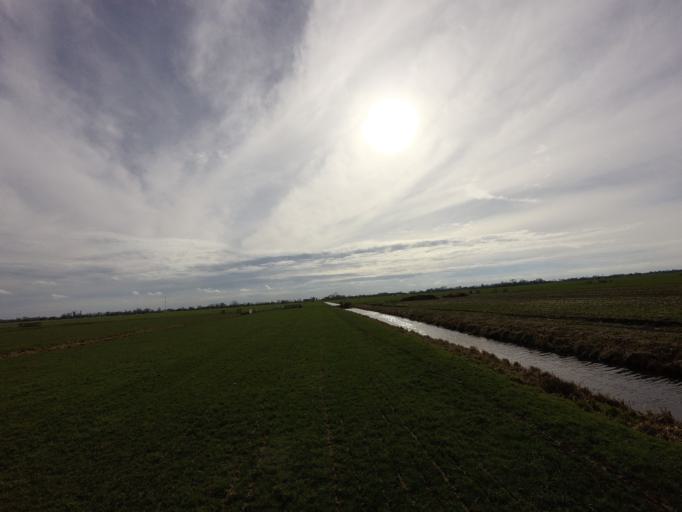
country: NL
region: Utrecht
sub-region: Gemeente Oudewater
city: Oudewater
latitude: 51.9963
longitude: 4.8753
